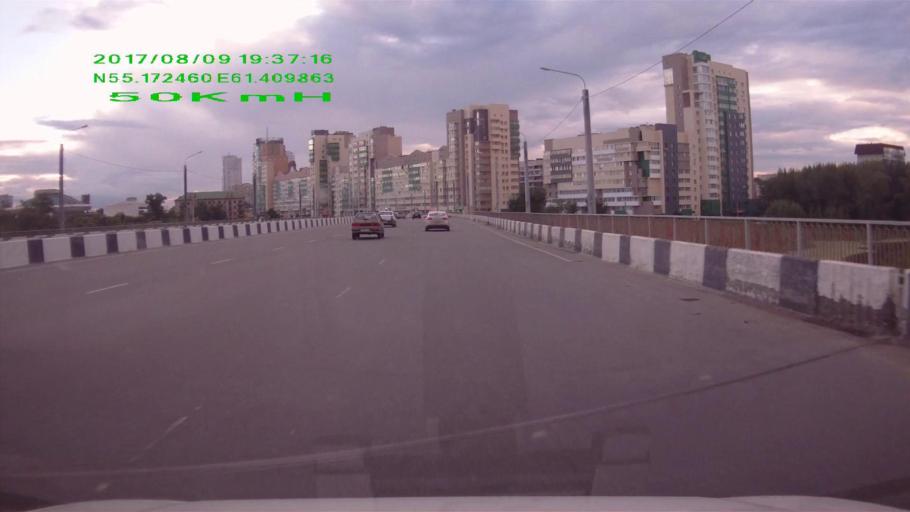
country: RU
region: Chelyabinsk
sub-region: Gorod Chelyabinsk
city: Chelyabinsk
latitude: 55.1726
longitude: 61.4084
